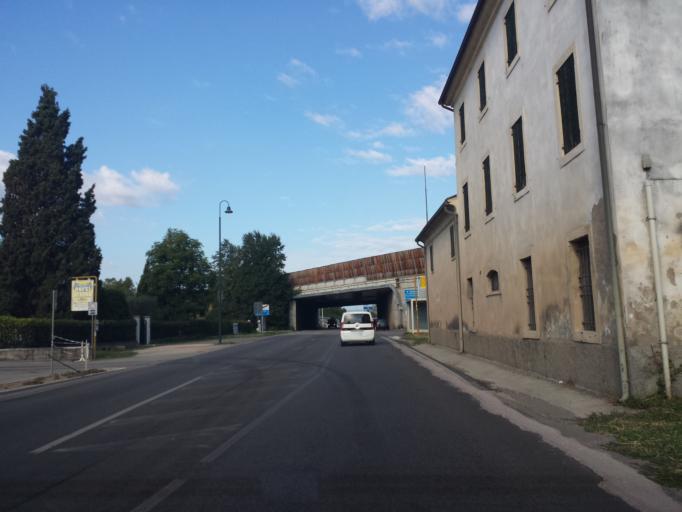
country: IT
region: Veneto
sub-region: Provincia di Verona
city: Monticelli-Fontana
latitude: 45.4203
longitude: 11.1237
